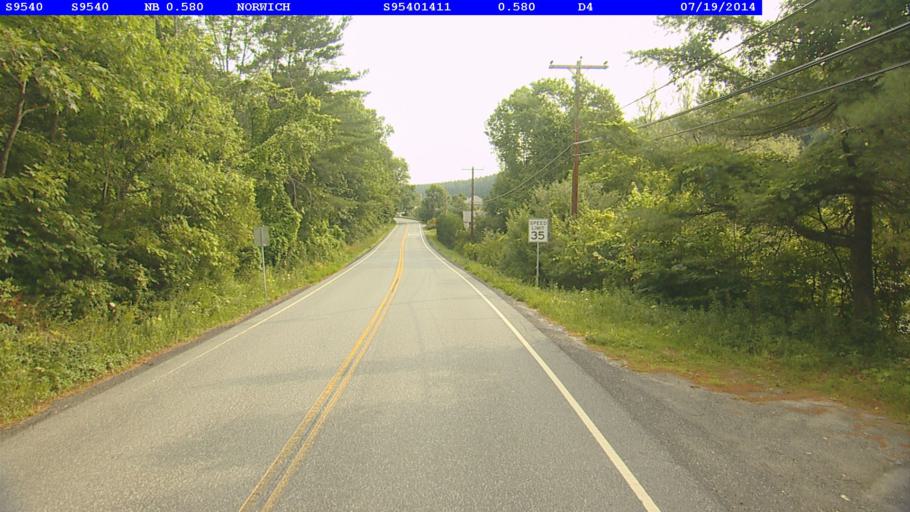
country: US
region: New Hampshire
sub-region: Grafton County
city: Hanover
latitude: 43.7102
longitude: -72.2943
